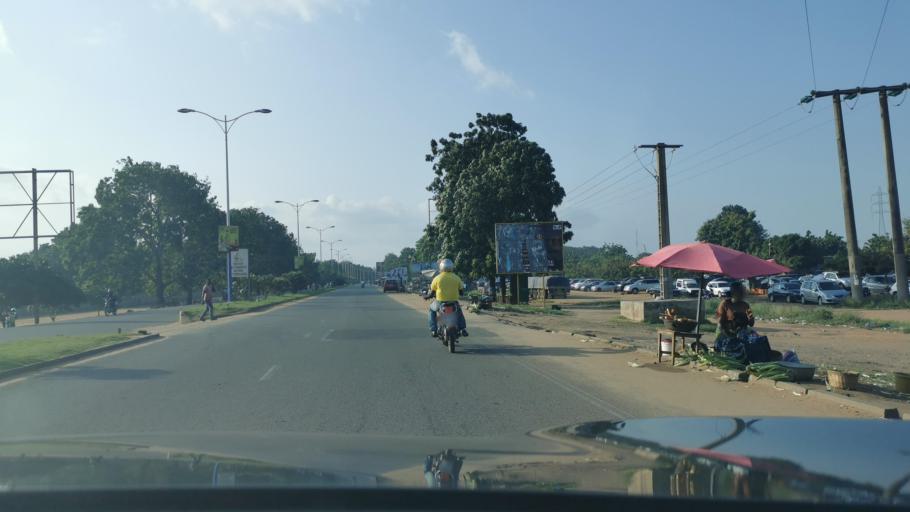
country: TG
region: Maritime
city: Lome
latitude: 6.1977
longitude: 1.2089
